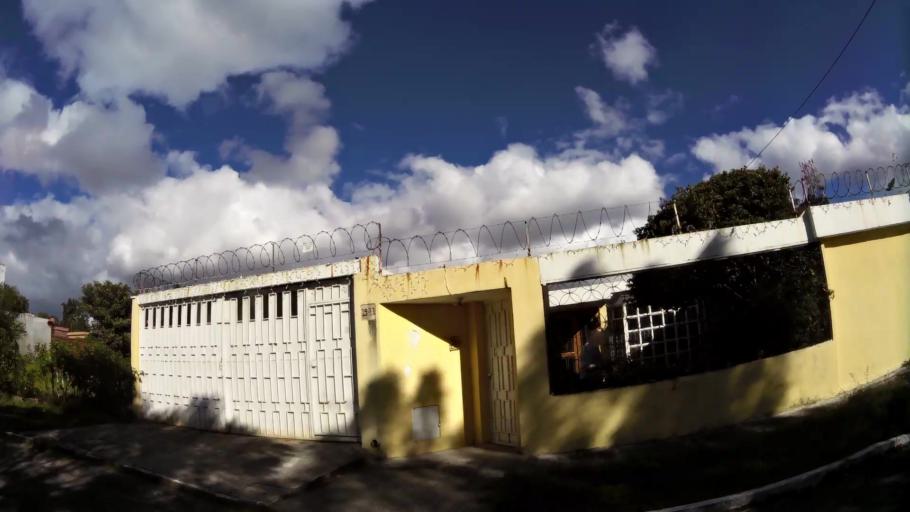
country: GT
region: Guatemala
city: Guatemala City
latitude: 14.6065
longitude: -90.5547
